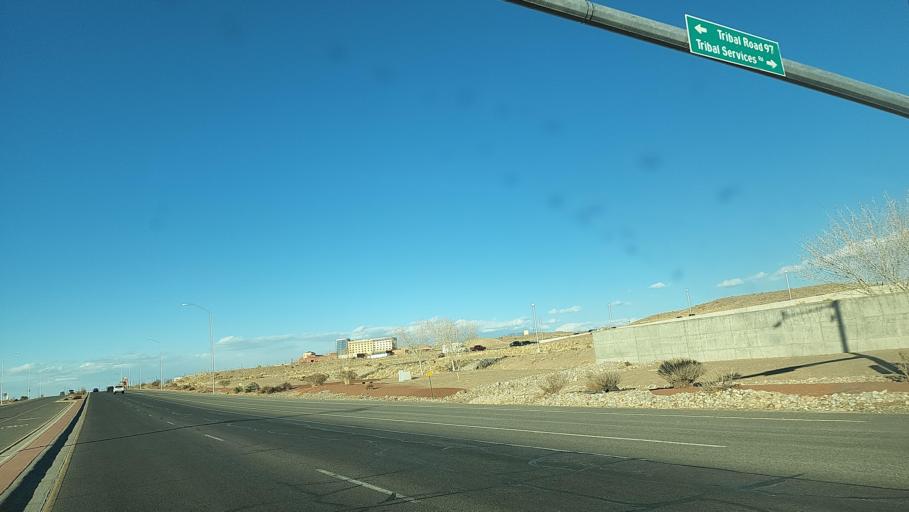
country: US
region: New Mexico
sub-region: Bernalillo County
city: South Valley
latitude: 34.9303
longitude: -106.6673
